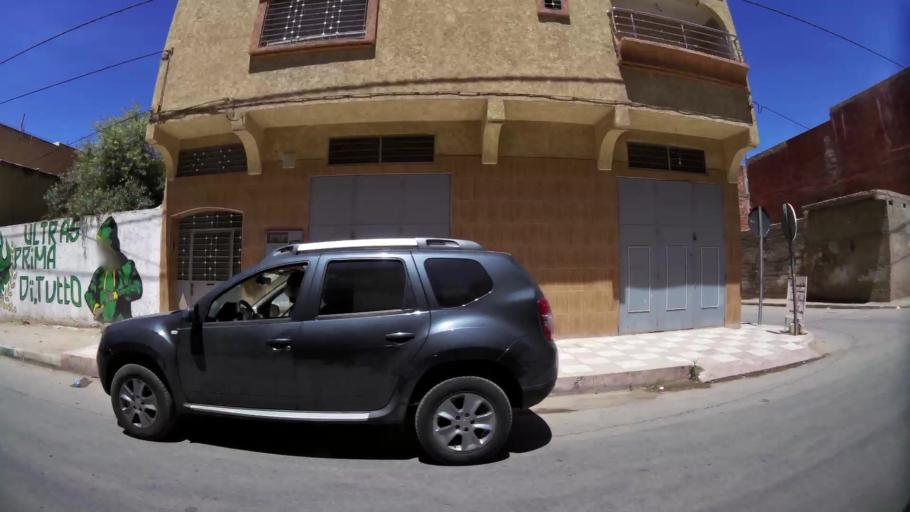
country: MA
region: Oriental
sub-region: Oujda-Angad
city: Oujda
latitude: 34.6595
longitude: -1.9216
